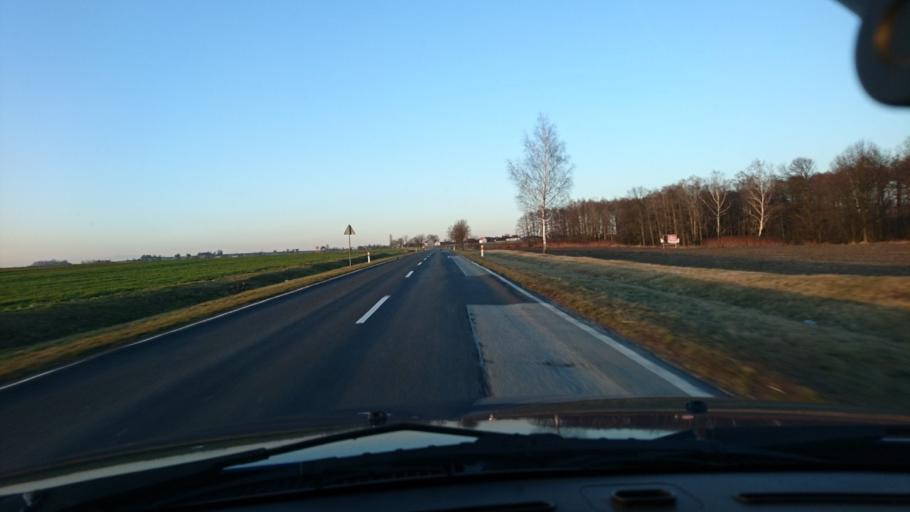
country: PL
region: Silesian Voivodeship
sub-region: Powiat gliwicki
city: Wielowies
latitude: 50.4622
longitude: 18.6109
